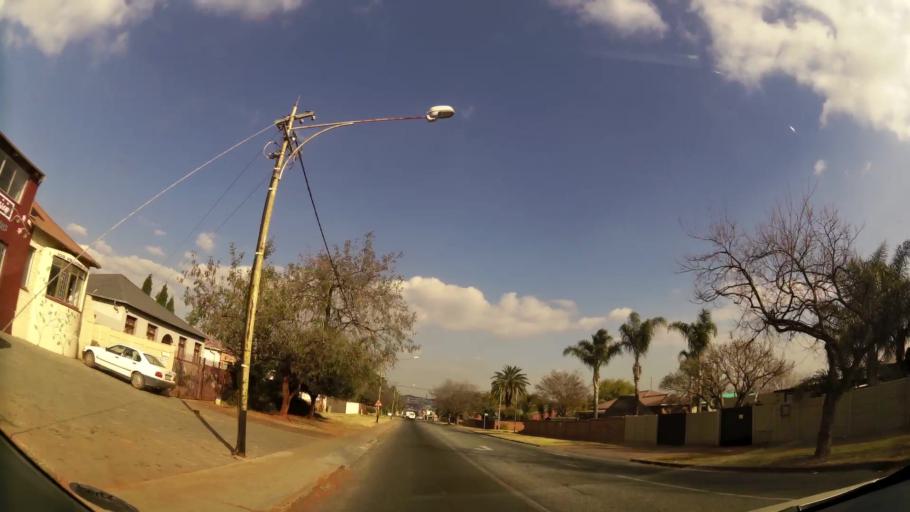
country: ZA
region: Gauteng
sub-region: West Rand District Municipality
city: Krugersdorp
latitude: -26.0883
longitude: 27.7681
